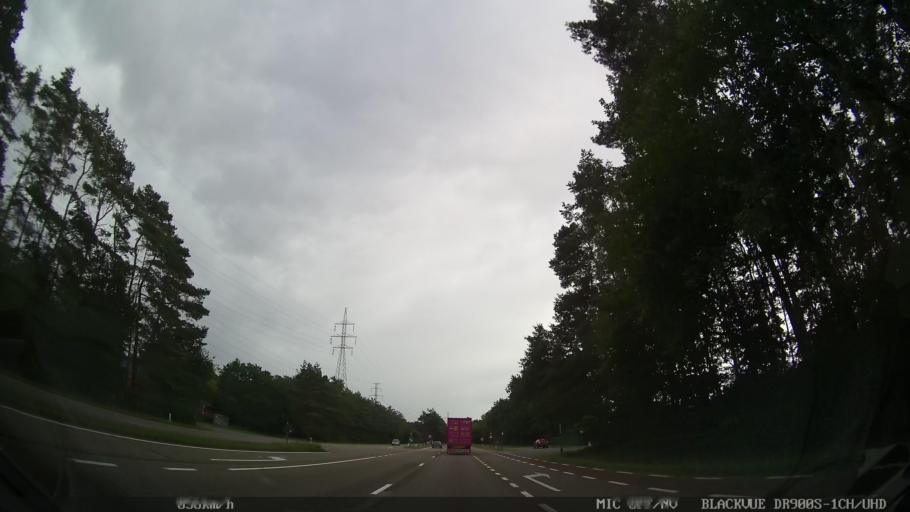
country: BE
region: Flanders
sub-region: Provincie Limburg
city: Genk
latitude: 50.9540
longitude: 5.5228
